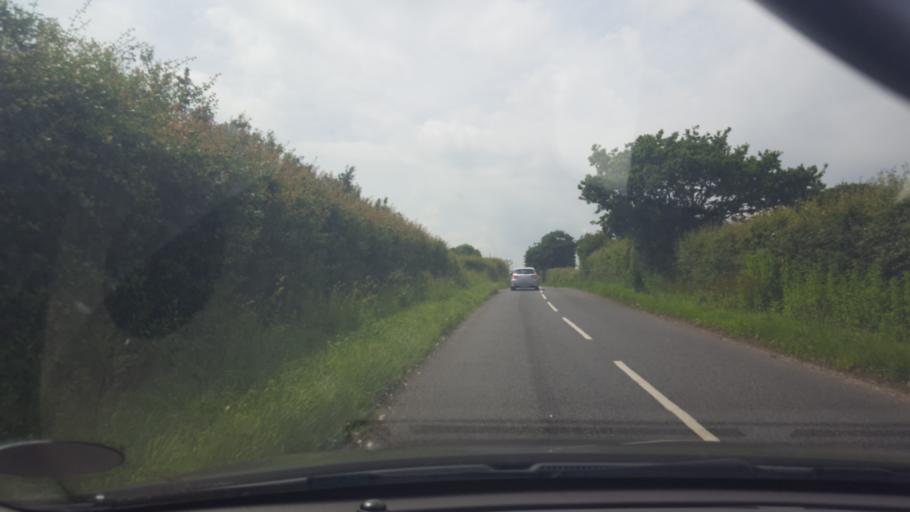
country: GB
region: England
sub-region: Essex
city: Clacton-on-Sea
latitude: 51.8125
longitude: 1.1837
